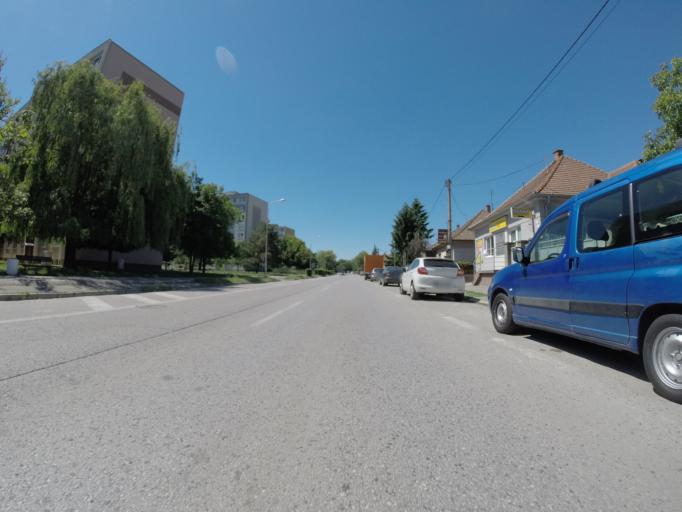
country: SK
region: Trnavsky
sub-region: Okres Galanta
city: Galanta
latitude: 48.1938
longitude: 17.7279
